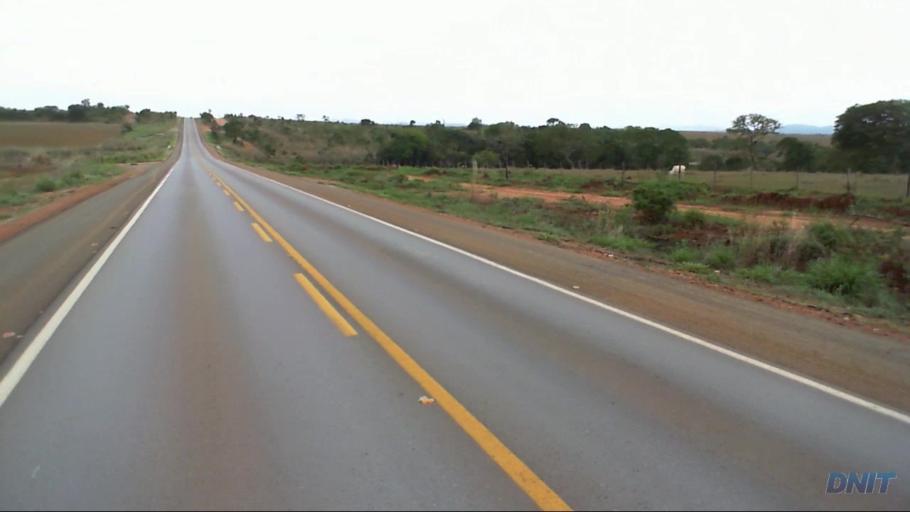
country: BR
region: Goias
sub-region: Uruacu
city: Uruacu
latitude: -14.6590
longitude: -49.1557
